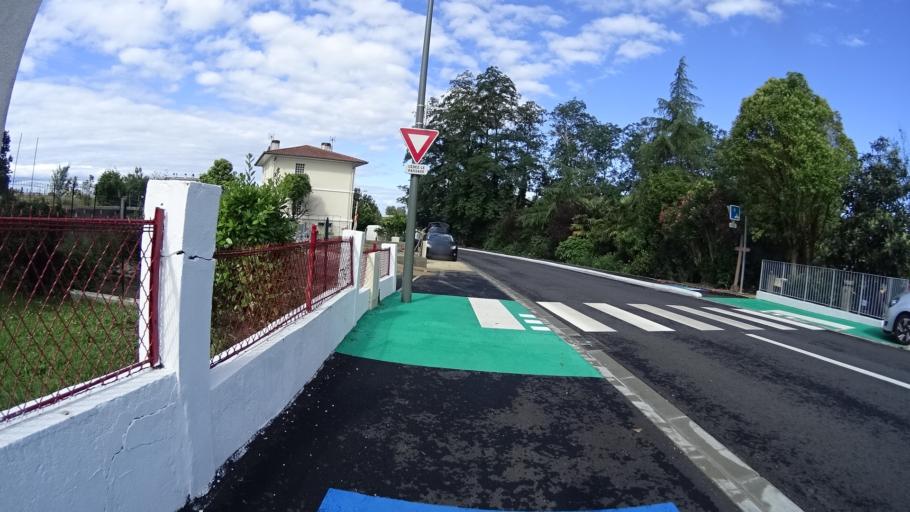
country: FR
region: Aquitaine
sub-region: Departement des Landes
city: Dax
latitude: 43.7012
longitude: -1.0666
